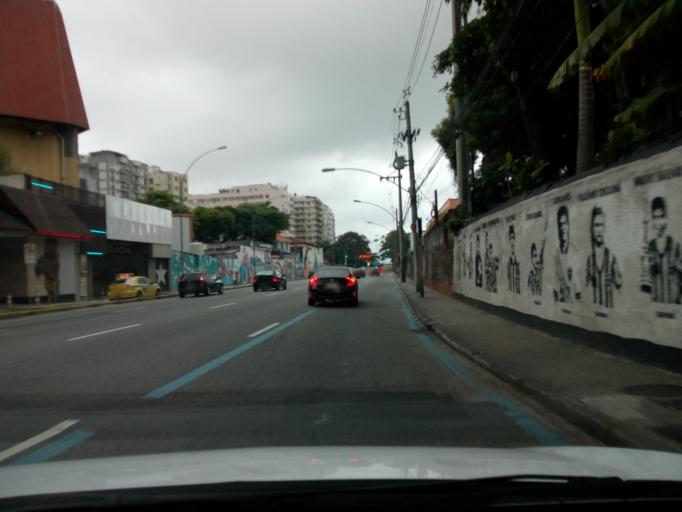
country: BR
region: Rio de Janeiro
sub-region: Rio De Janeiro
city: Rio de Janeiro
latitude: -22.9546
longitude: -43.1773
